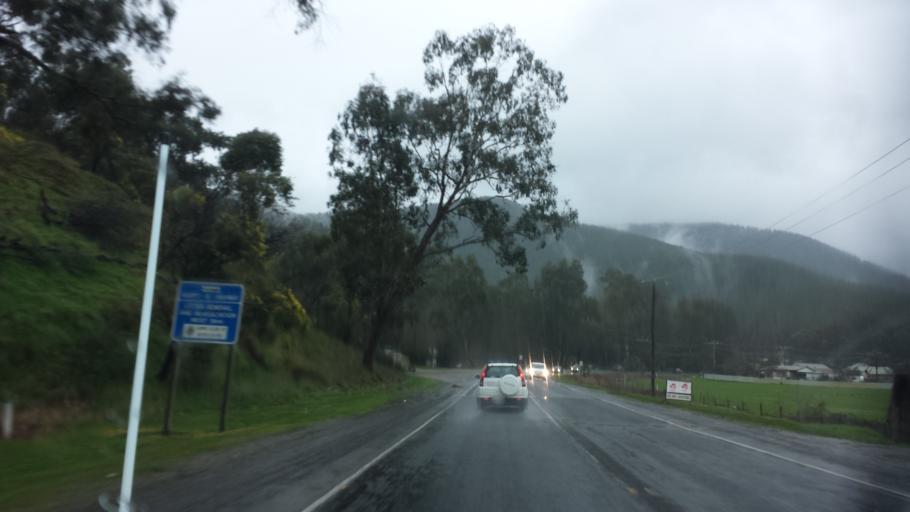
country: AU
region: Victoria
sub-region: Wangaratta
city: Wangaratta
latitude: -36.5703
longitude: 146.7335
